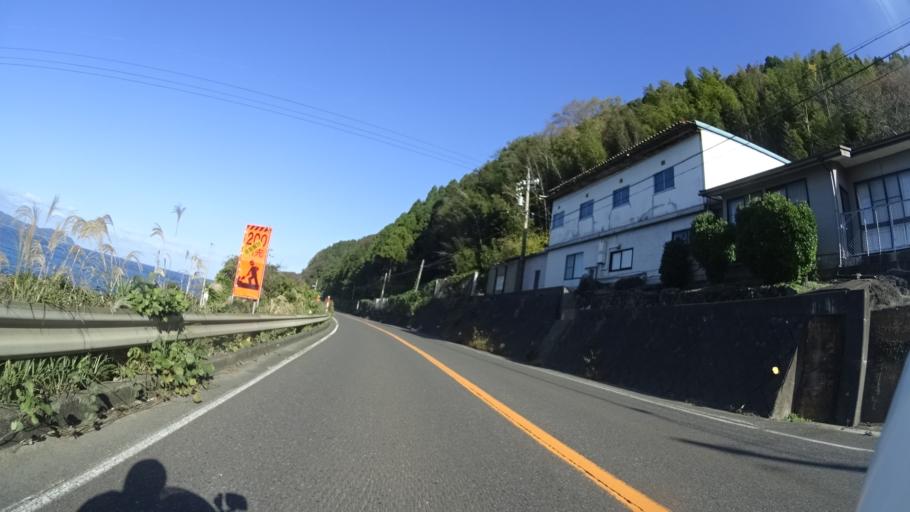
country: JP
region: Fukui
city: Tsuruga
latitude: 35.7254
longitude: 136.0997
